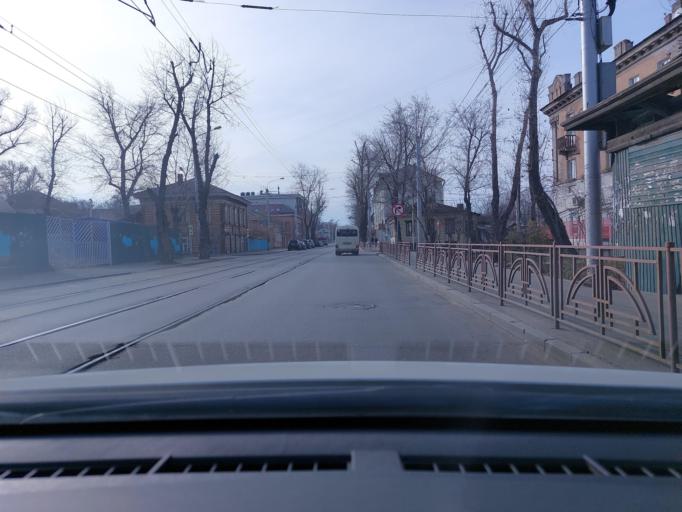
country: RU
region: Irkutsk
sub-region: Irkutskiy Rayon
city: Irkutsk
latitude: 52.2791
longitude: 104.2923
